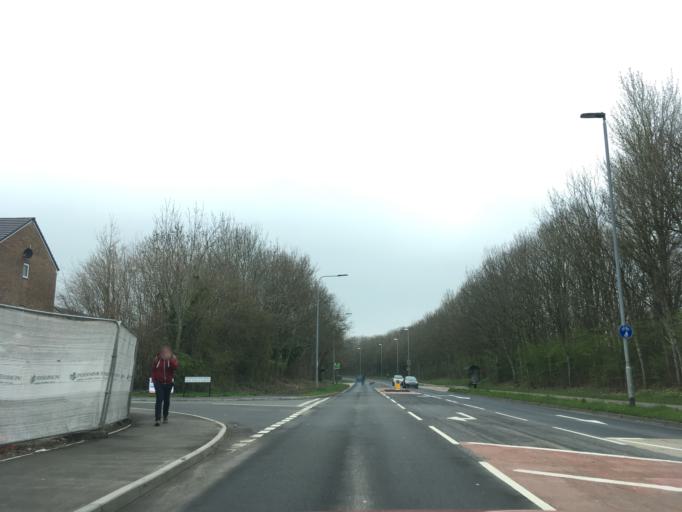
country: GB
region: Wales
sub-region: Newport
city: Newport
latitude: 51.5565
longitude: -3.0261
